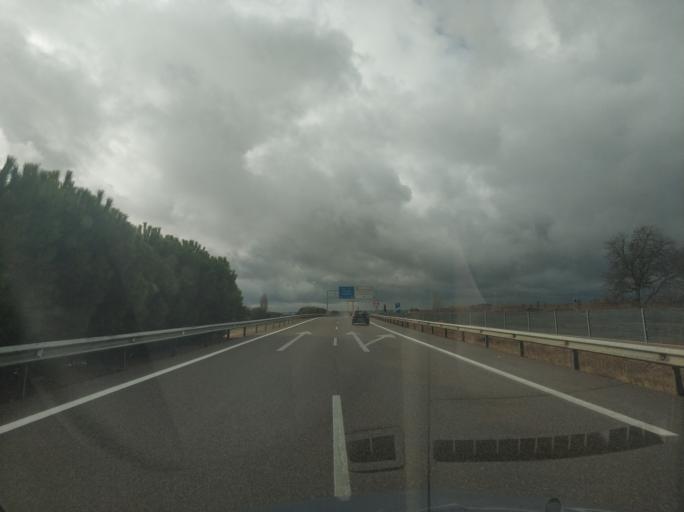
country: ES
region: Castille and Leon
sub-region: Provincia de Palencia
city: Reinoso de Cerrato
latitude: 42.0065
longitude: -4.3637
